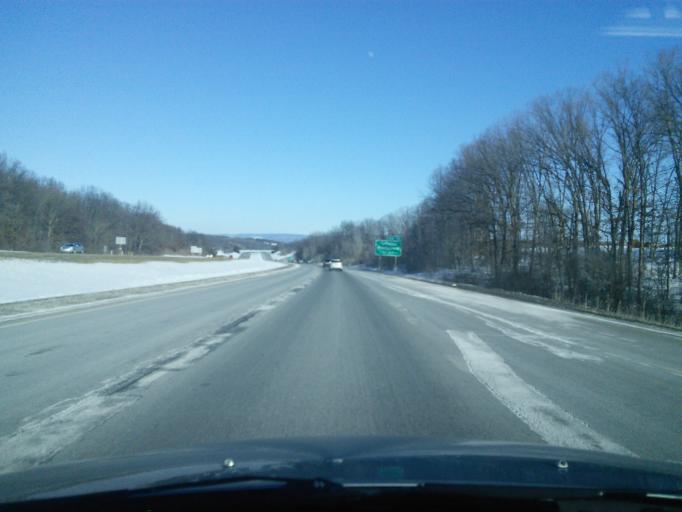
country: US
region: Pennsylvania
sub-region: Centre County
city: Park Forest Village
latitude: 40.8155
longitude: -77.9142
